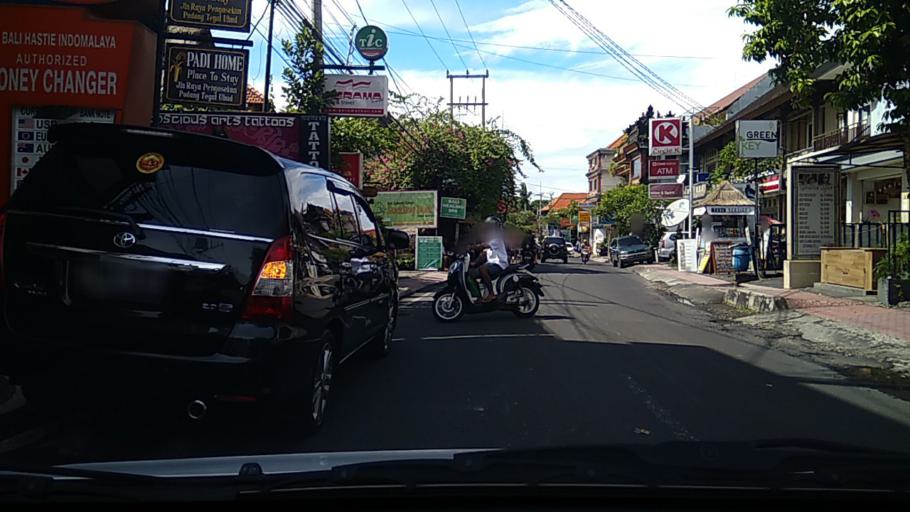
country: ID
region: Bali
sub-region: Kabupaten Gianyar
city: Ubud
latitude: -8.5194
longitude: 115.2632
